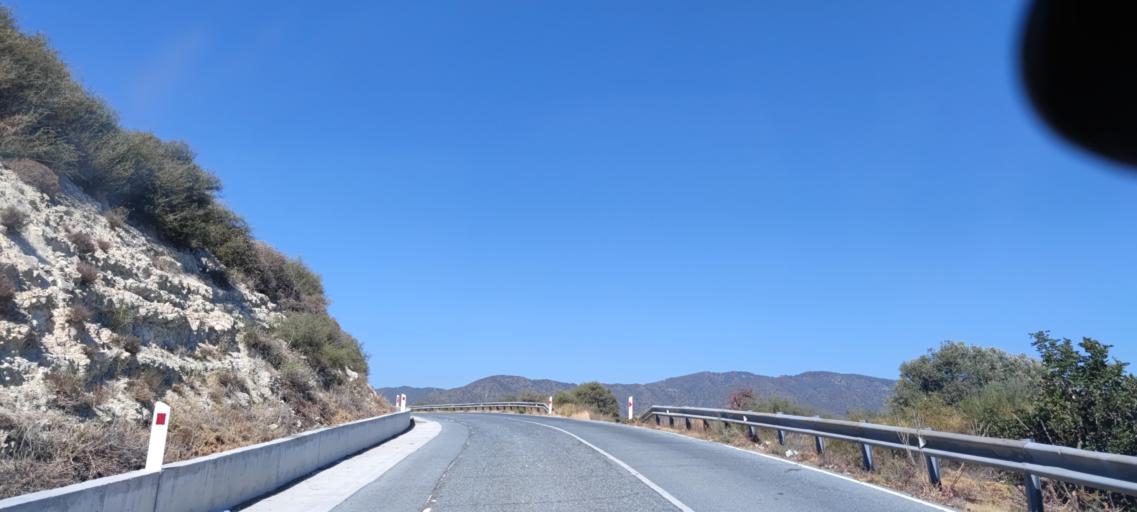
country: CY
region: Limassol
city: Mouttagiaka
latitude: 34.7641
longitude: 33.0599
